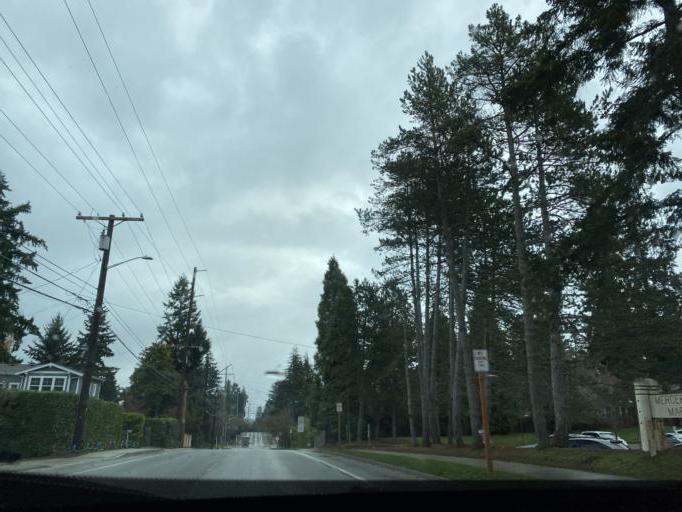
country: US
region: Washington
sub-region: King County
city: Mercer Island
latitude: 47.5745
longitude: -122.2212
